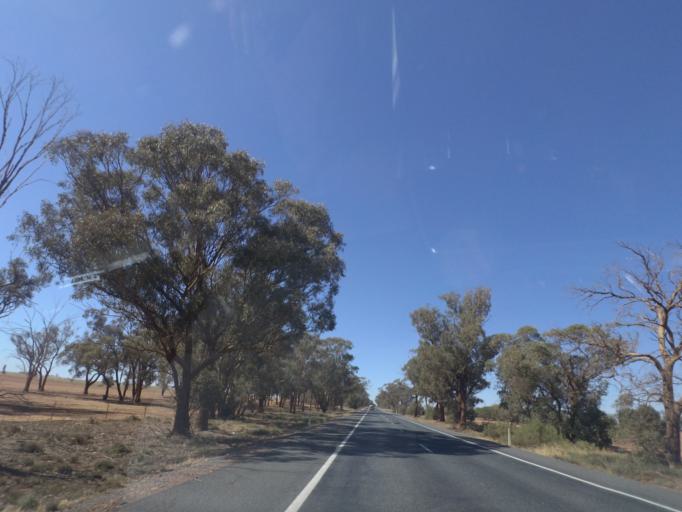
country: AU
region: New South Wales
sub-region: Bland
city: West Wyalong
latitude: -34.2053
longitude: 147.1097
